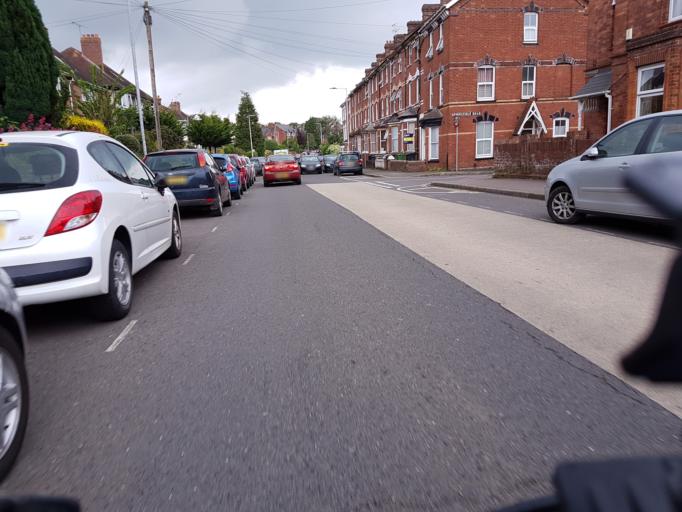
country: GB
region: England
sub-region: Devon
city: Exeter
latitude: 50.7339
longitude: -3.5227
